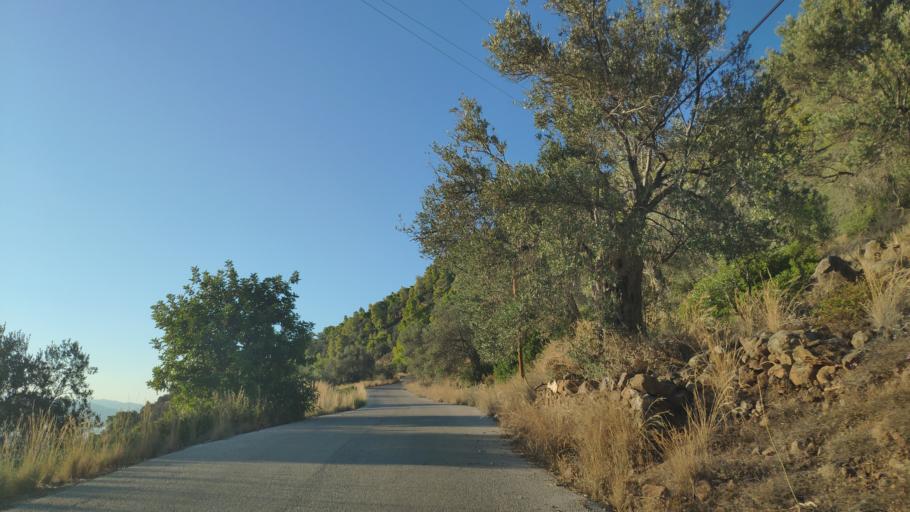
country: GR
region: Attica
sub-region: Nomos Piraios
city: Megalochori
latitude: 37.6005
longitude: 23.3356
